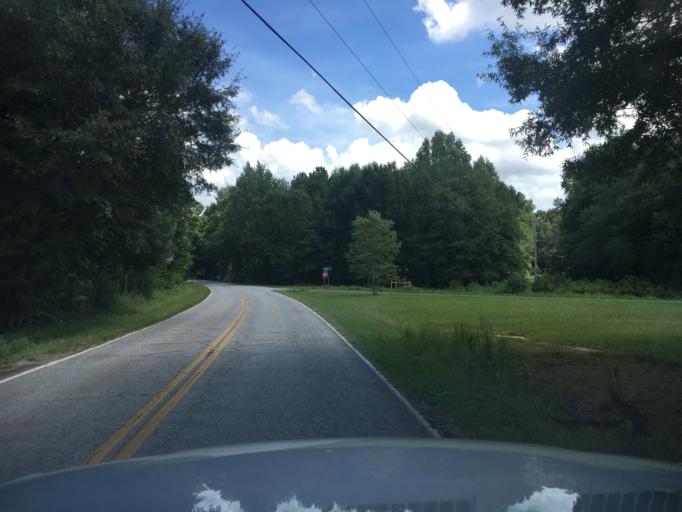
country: US
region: South Carolina
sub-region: Anderson County
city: Belton
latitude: 34.5668
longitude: -82.4832
